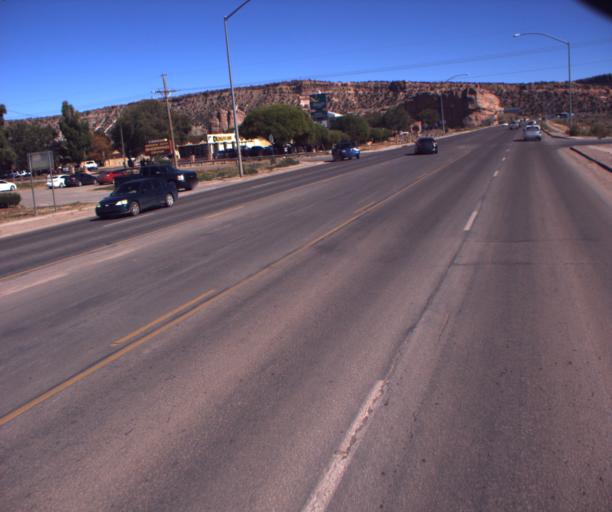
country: US
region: Arizona
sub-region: Apache County
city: Window Rock
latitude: 35.6633
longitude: -109.0552
